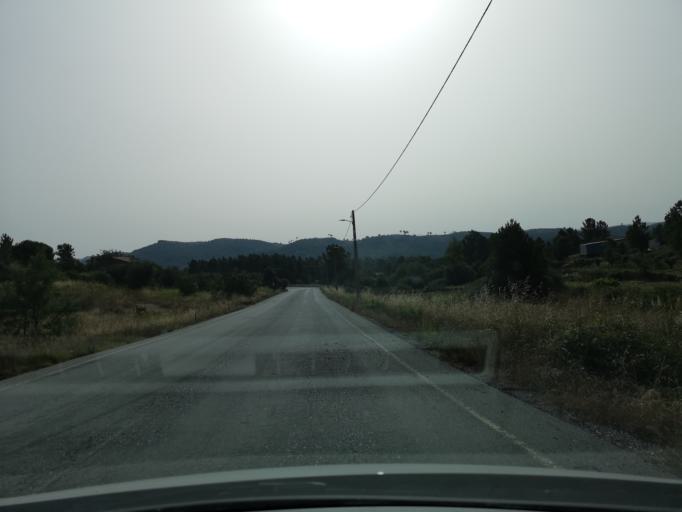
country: PT
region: Castelo Branco
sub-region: Belmonte
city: Belmonte
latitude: 40.3741
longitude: -7.3205
